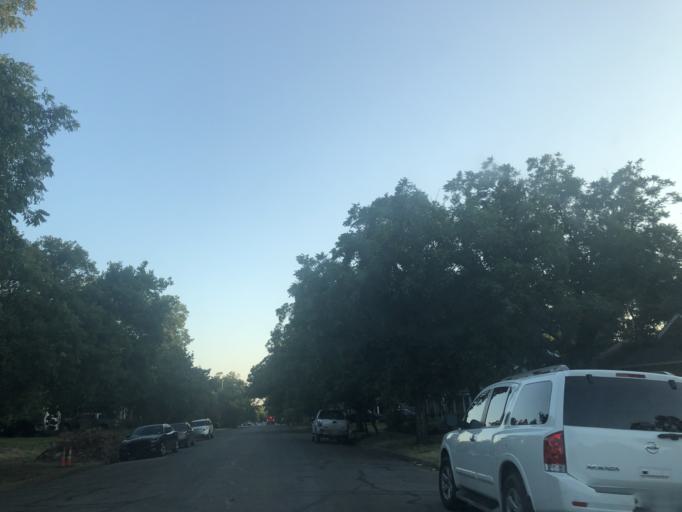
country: US
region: Texas
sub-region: Dallas County
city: Dallas
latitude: 32.7507
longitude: -96.8266
